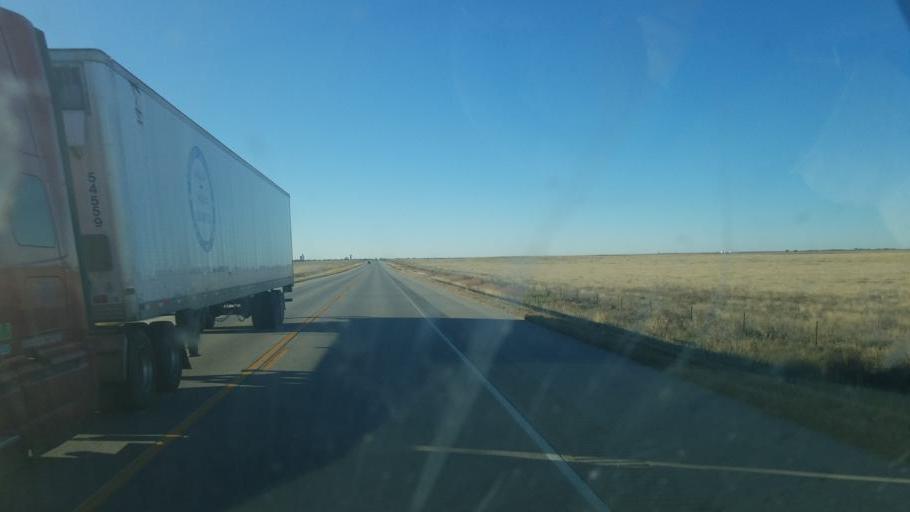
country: US
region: Colorado
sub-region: Kiowa County
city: Eads
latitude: 38.5221
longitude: -102.7858
